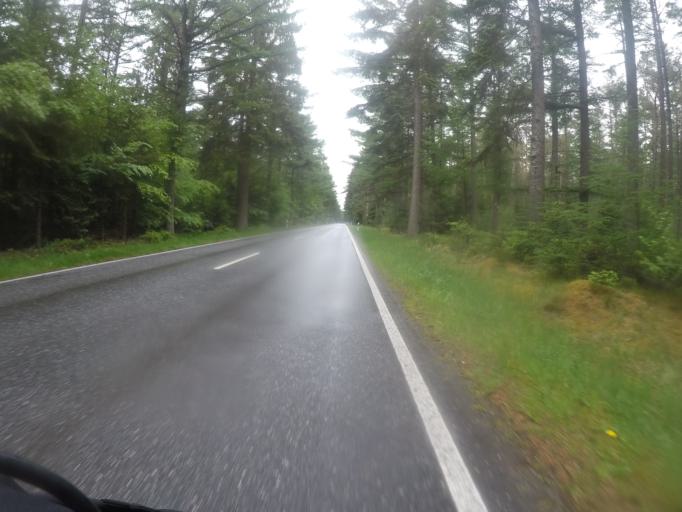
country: DE
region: Schleswig-Holstein
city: Hartenholm
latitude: 53.9260
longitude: 10.0898
